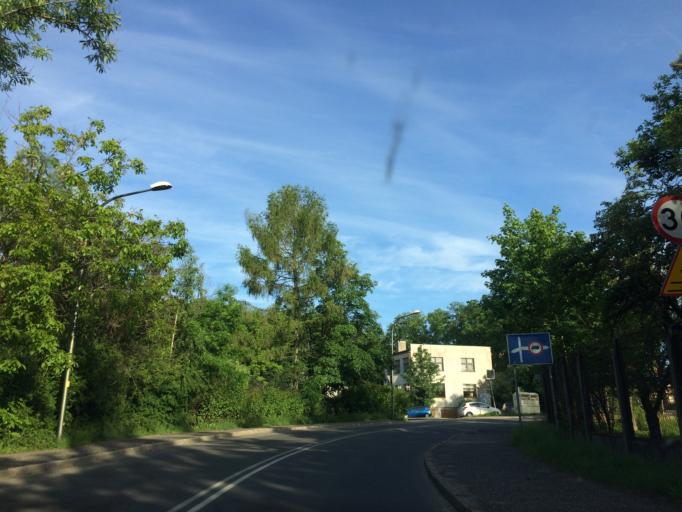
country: PL
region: Lower Silesian Voivodeship
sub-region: Powiat swidnicki
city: Swidnica
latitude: 50.8413
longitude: 16.4724
